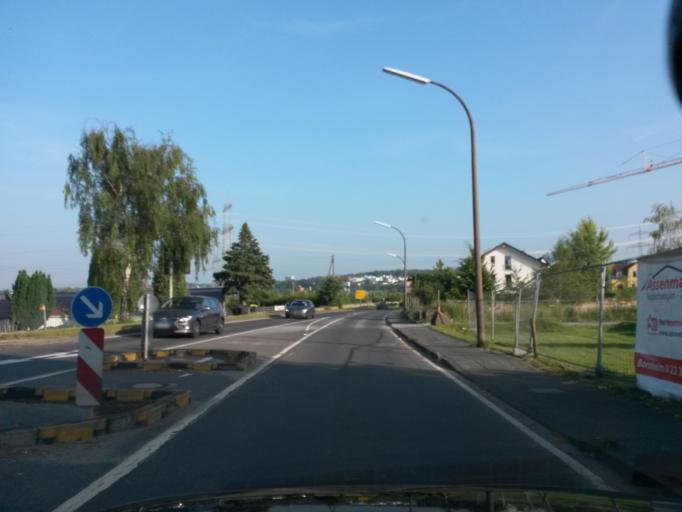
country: DE
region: North Rhine-Westphalia
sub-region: Regierungsbezirk Koln
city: Alfter
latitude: 50.7214
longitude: 7.0283
